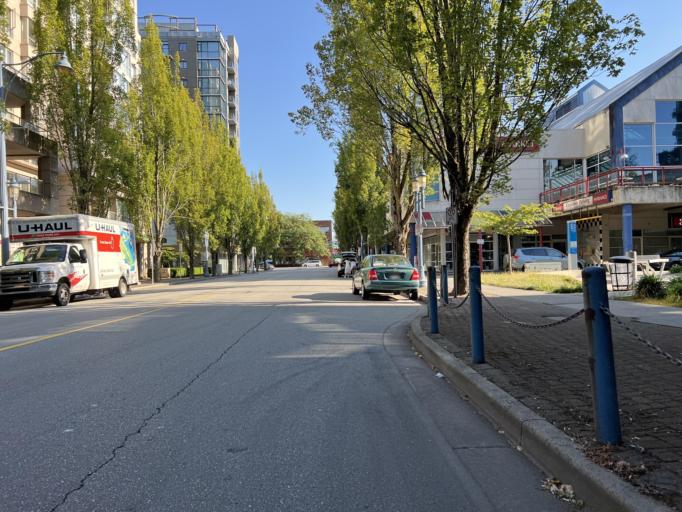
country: CA
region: British Columbia
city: Richmond
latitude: 49.1691
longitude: -123.1336
